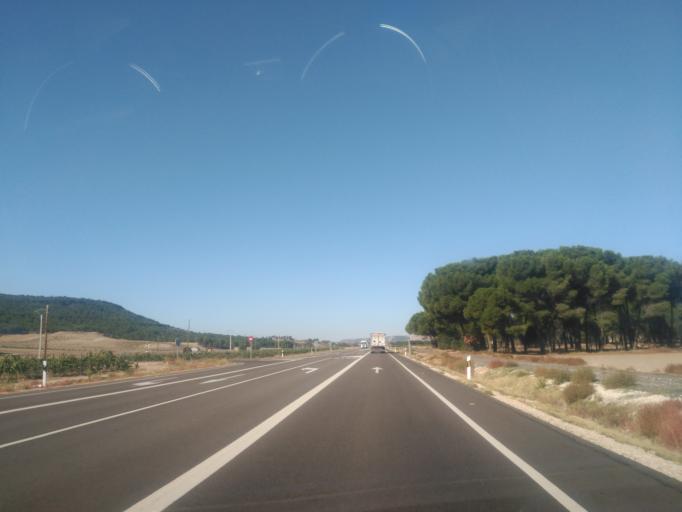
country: ES
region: Castille and Leon
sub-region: Provincia de Valladolid
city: Quintanilla de Onesimo
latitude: 41.6276
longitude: -4.3274
